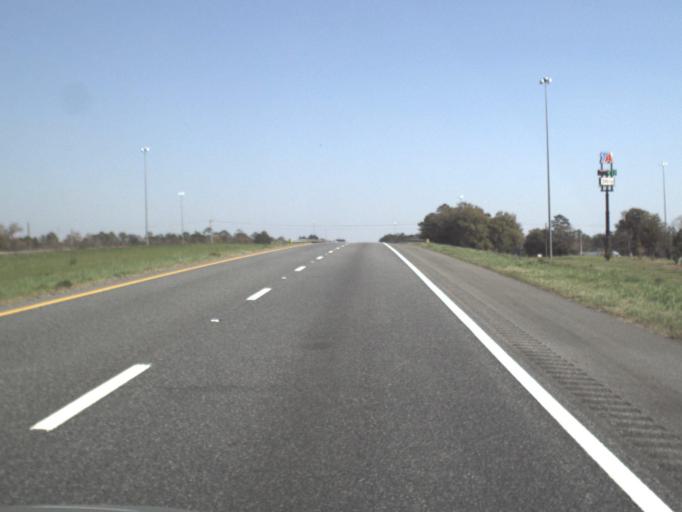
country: US
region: Florida
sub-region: Jackson County
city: Marianna
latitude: 30.7218
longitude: -85.1882
